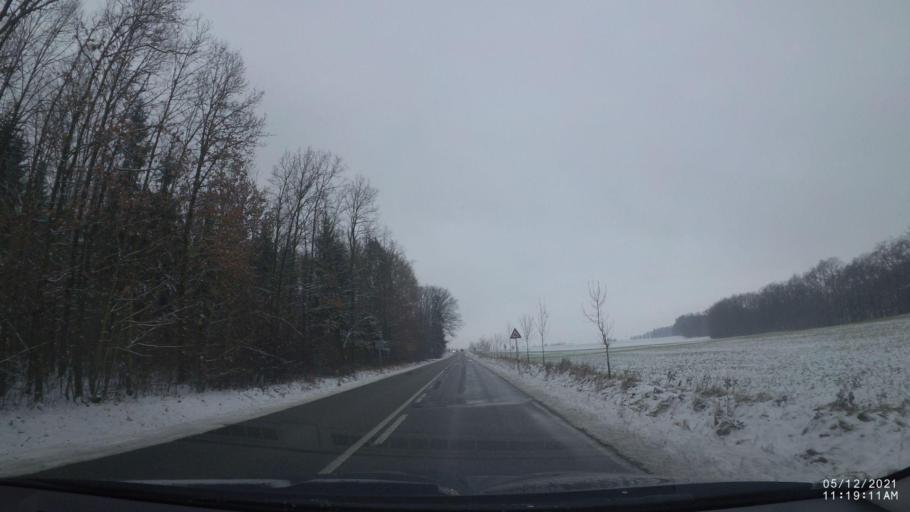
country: CZ
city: Solnice
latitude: 50.1929
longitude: 16.2288
